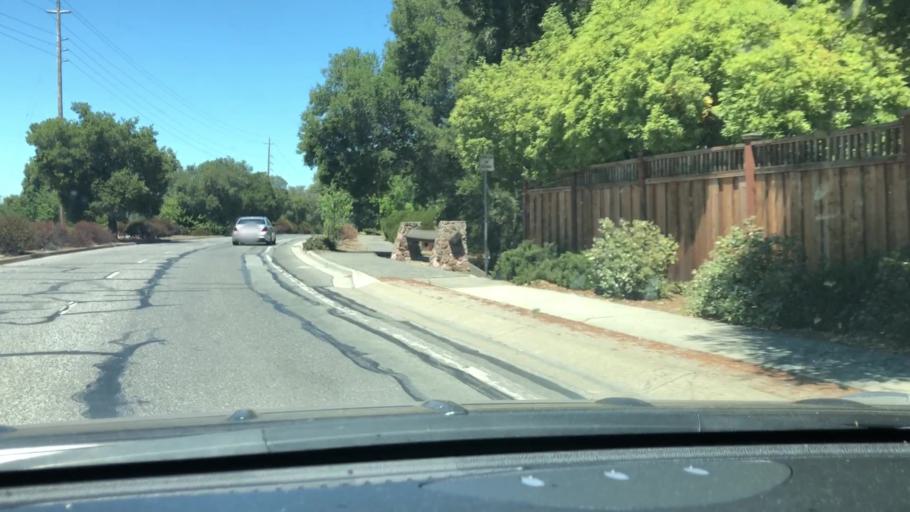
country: US
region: California
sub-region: Santa Clara County
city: Saratoga
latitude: 37.2683
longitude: -122.0138
